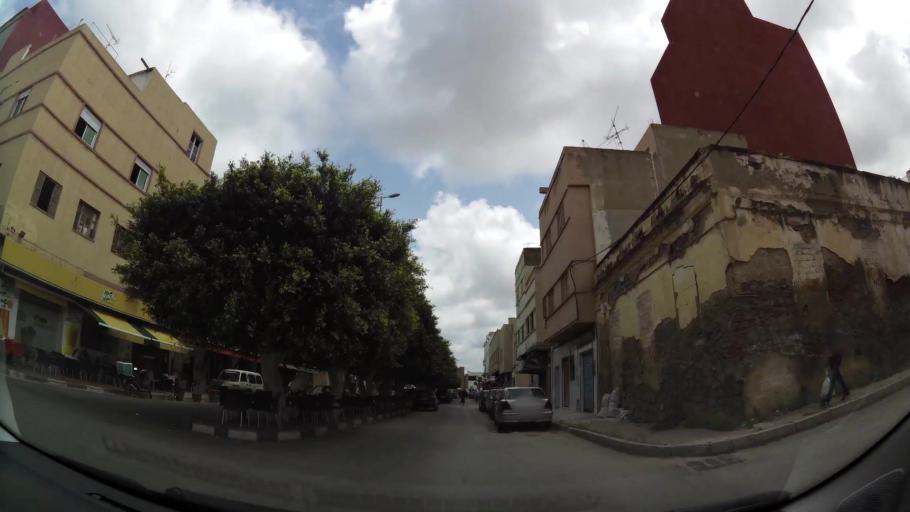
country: MA
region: Oriental
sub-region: Nador
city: Nador
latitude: 35.1789
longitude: -2.9241
